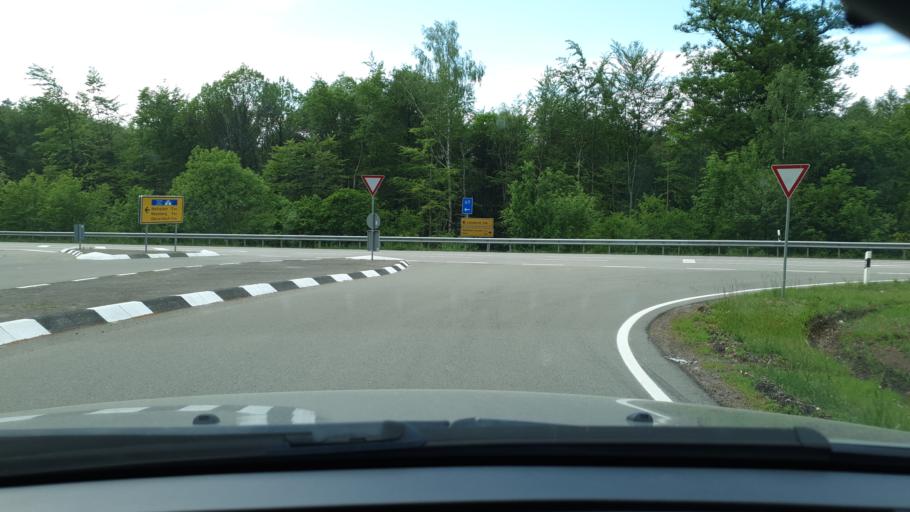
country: DE
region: Rheinland-Pfalz
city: Landstuhl
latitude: 49.4046
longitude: 7.5894
